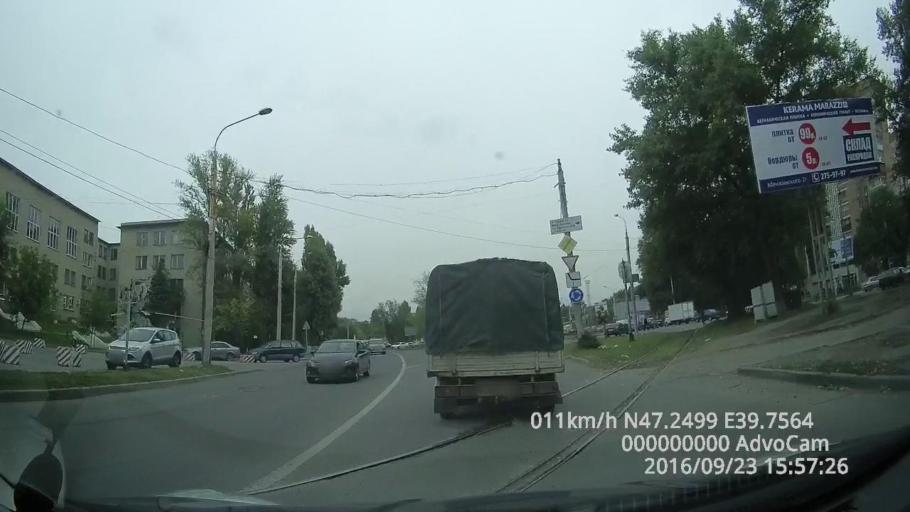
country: RU
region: Rostov
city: Imeni Chkalova
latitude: 47.2499
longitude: 39.7564
